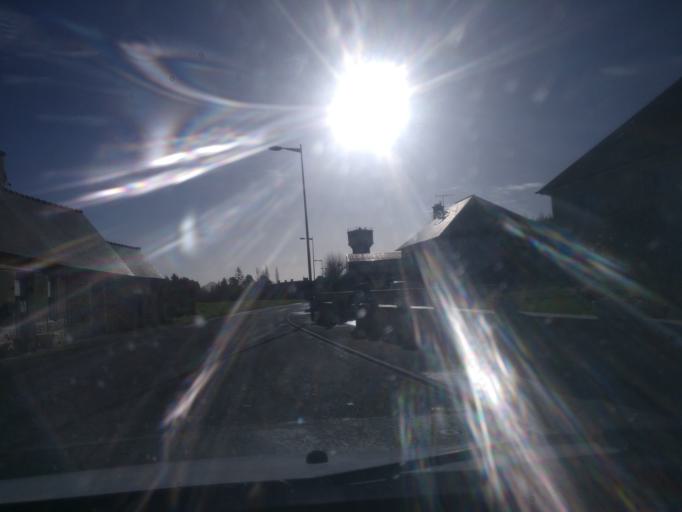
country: FR
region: Brittany
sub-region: Departement d'Ille-et-Vilaine
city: Pleine-Fougeres
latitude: 48.5370
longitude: -1.5666
